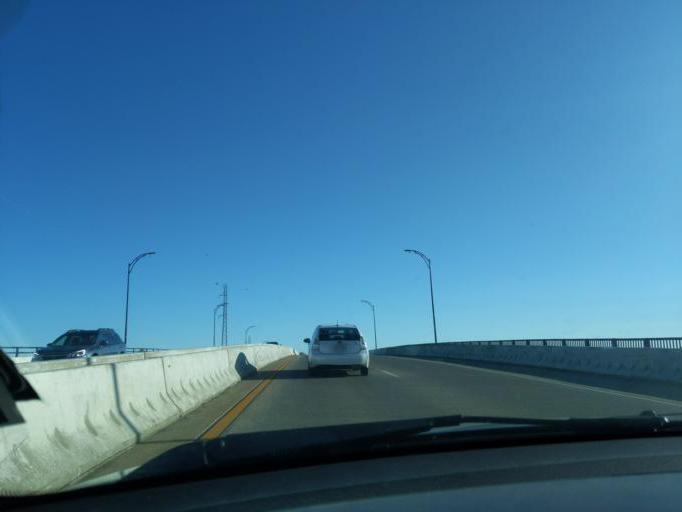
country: US
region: Massachusetts
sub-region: Essex County
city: Salem
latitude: 42.5380
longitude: -70.8879
